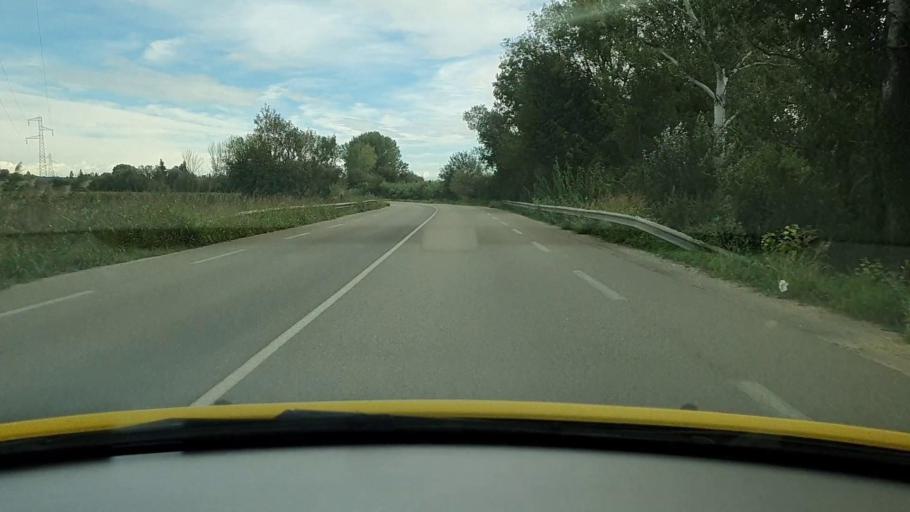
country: FR
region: Languedoc-Roussillon
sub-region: Departement du Gard
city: Bellegarde
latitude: 43.7491
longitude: 4.5277
